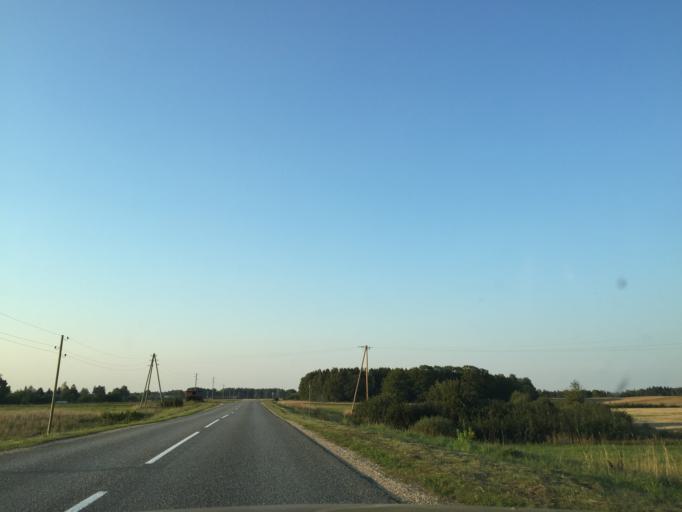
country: LV
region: Limbazu Rajons
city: Limbazi
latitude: 57.5731
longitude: 24.7706
